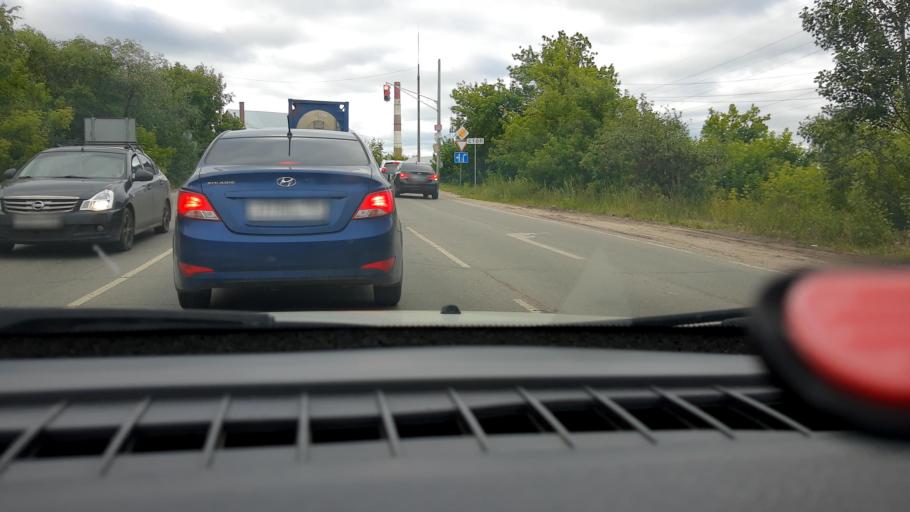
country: RU
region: Nizjnij Novgorod
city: Dzerzhinsk
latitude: 56.2425
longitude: 43.5079
